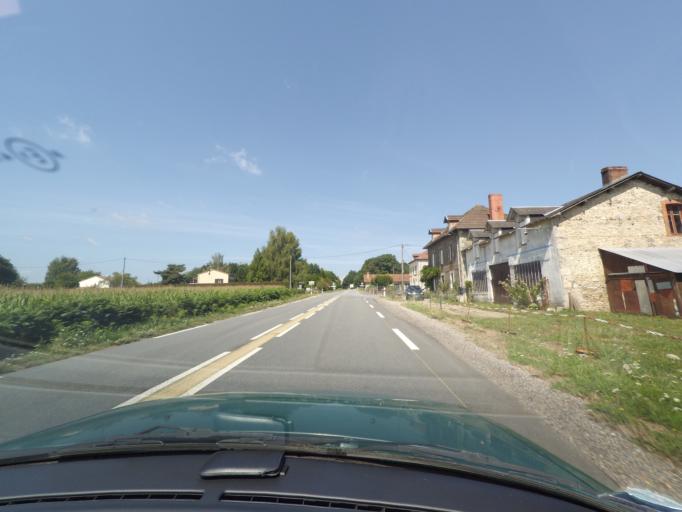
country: FR
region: Limousin
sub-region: Departement de la Haute-Vienne
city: Saint-Paul
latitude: 45.7871
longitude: 1.4709
